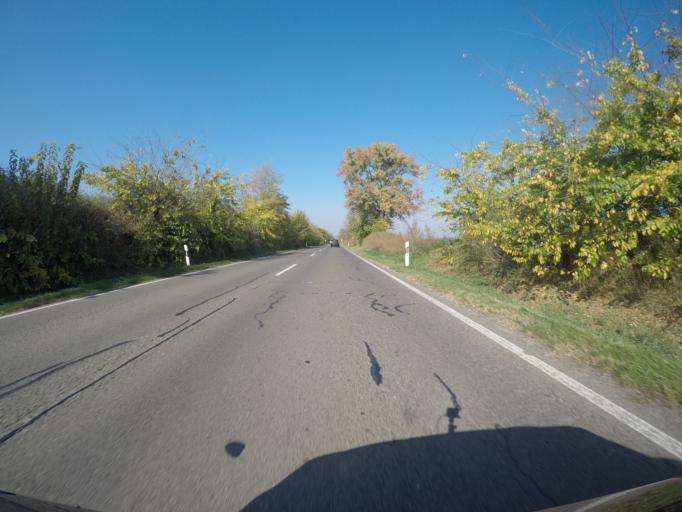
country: HU
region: Tolna
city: Tengelic
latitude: 46.5238
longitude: 18.6599
